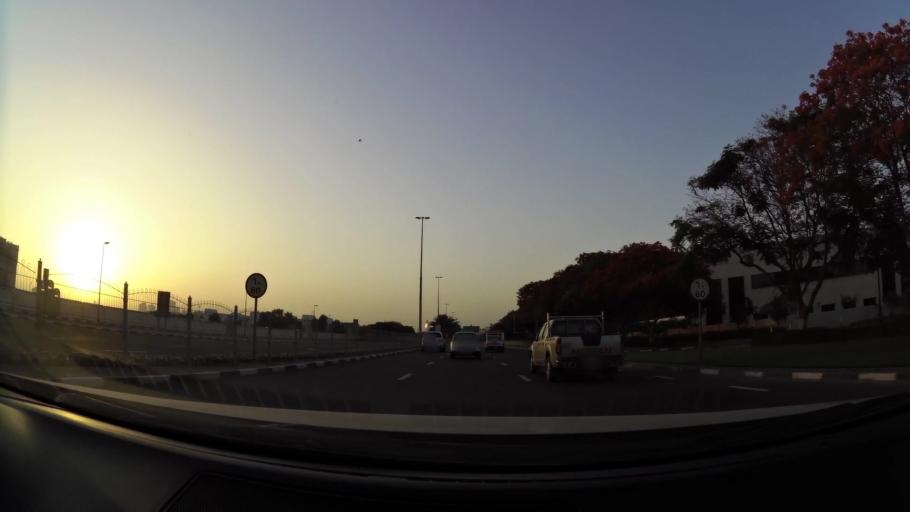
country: AE
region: Ash Shariqah
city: Sharjah
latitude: 25.2362
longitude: 55.3250
